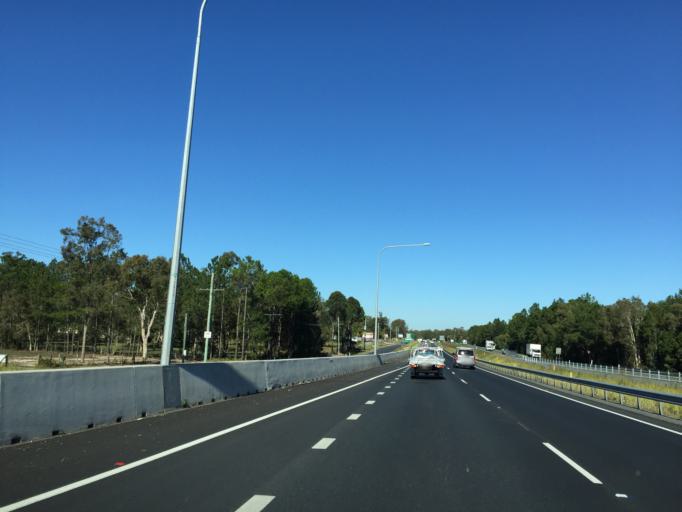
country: AU
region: Queensland
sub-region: Moreton Bay
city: Caboolture
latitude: -27.0472
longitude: 152.9776
